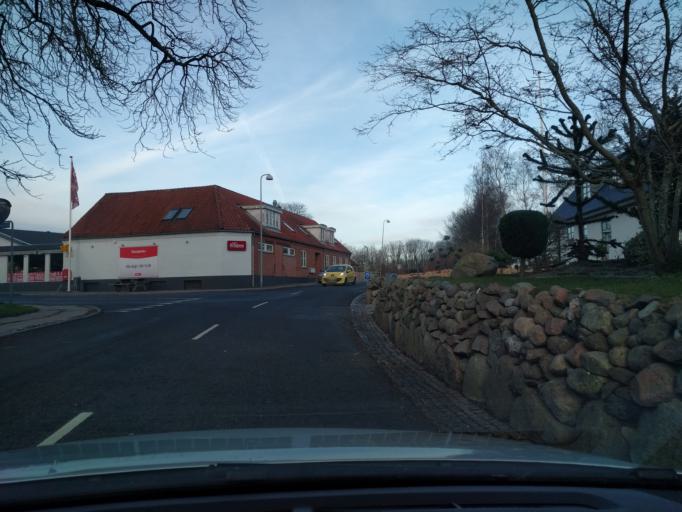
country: DK
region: South Denmark
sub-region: Odense Kommune
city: Neder Holluf
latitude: 55.3577
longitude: 10.4928
